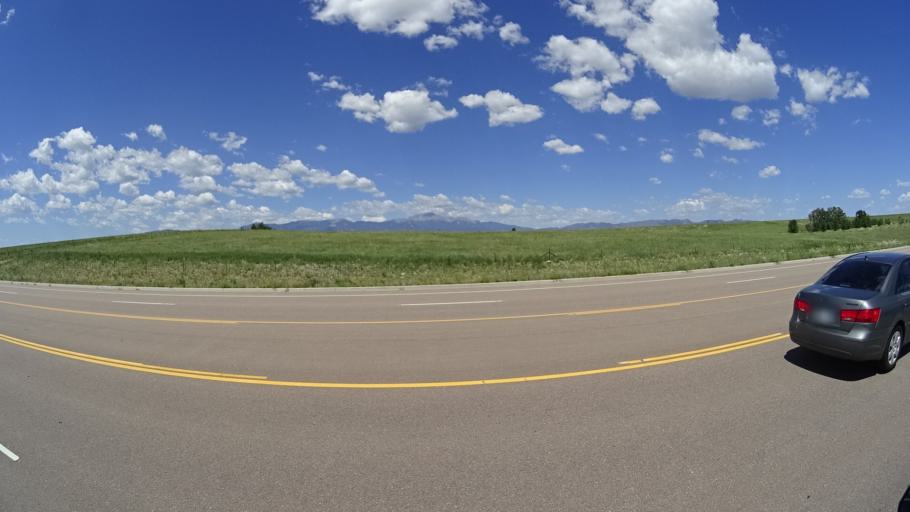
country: US
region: Colorado
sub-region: El Paso County
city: Cimarron Hills
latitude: 38.8448
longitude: -104.6828
